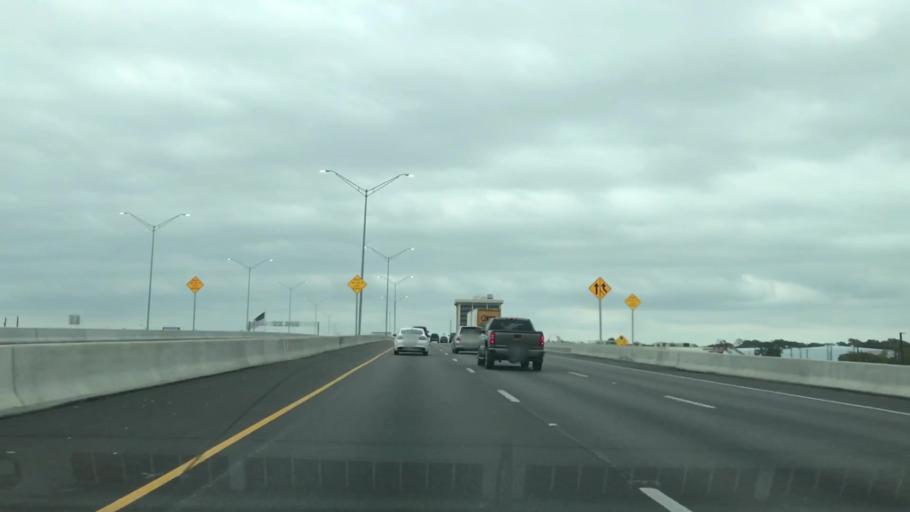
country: US
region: Texas
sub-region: Dallas County
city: Irving
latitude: 32.8366
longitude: -96.9617
